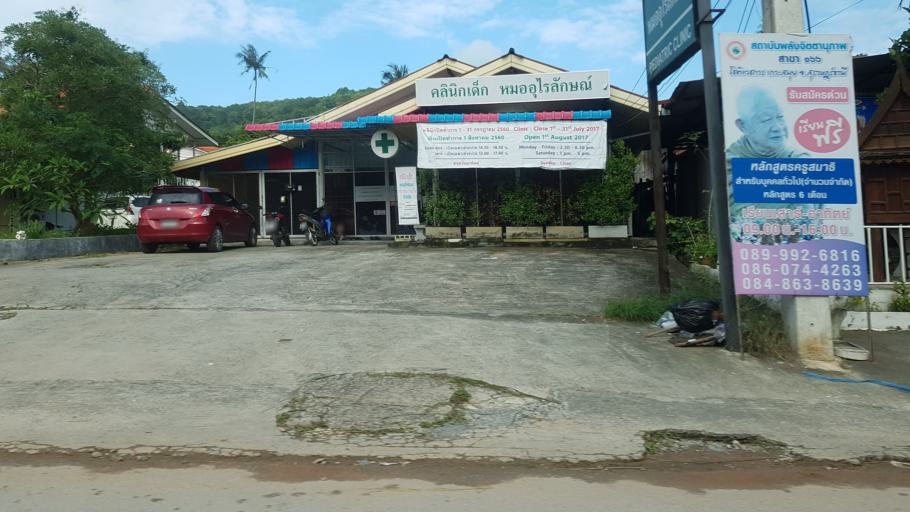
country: TH
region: Surat Thani
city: Ko Samui
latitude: 9.5476
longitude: 100.0375
